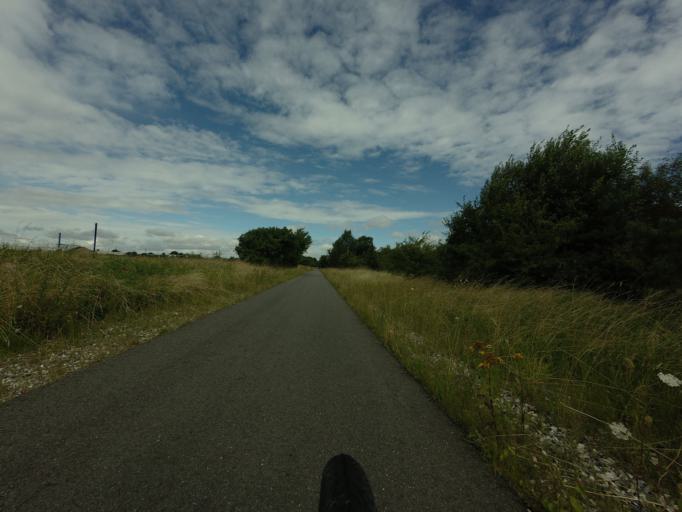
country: DK
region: Central Jutland
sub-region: Norddjurs Kommune
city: Auning
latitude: 56.4228
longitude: 10.3835
